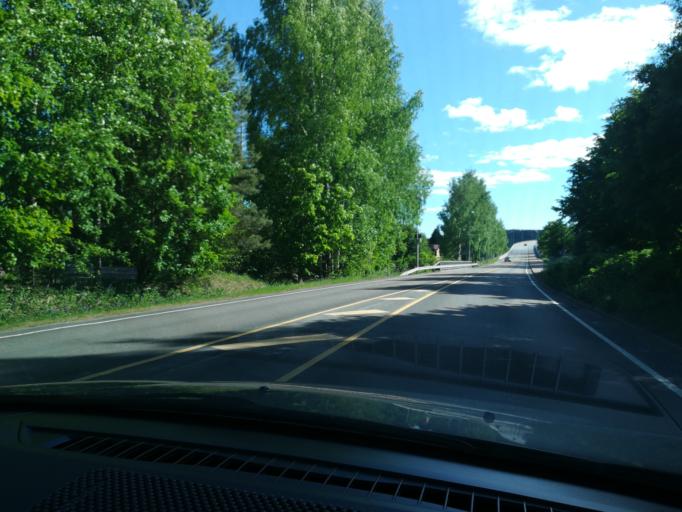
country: FI
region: Southern Savonia
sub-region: Mikkeli
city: Puumala
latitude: 61.5243
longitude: 28.1817
